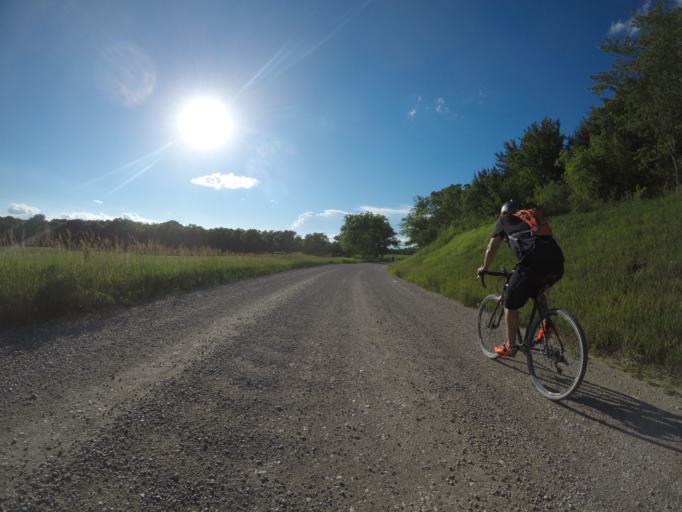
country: US
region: Kansas
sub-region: Riley County
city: Ogden
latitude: 39.2392
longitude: -96.7304
